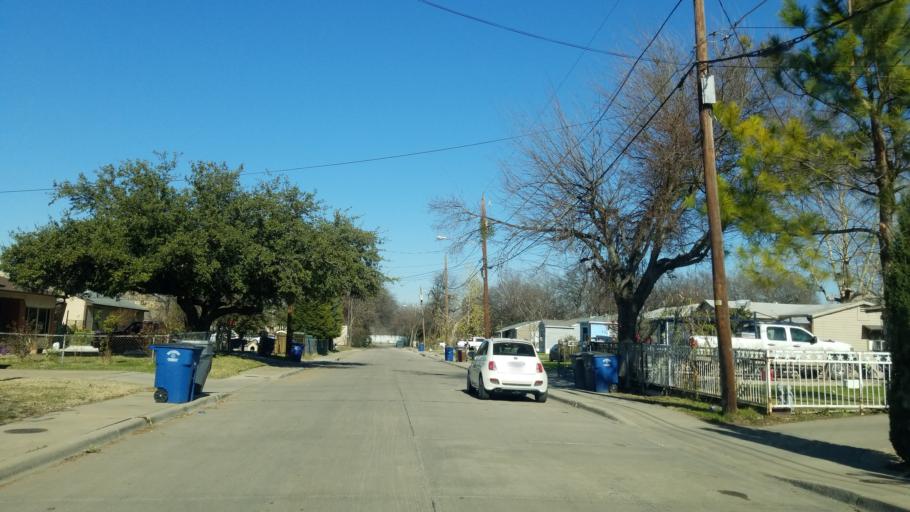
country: US
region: Texas
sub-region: Dallas County
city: Cockrell Hill
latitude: 32.7565
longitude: -96.9154
